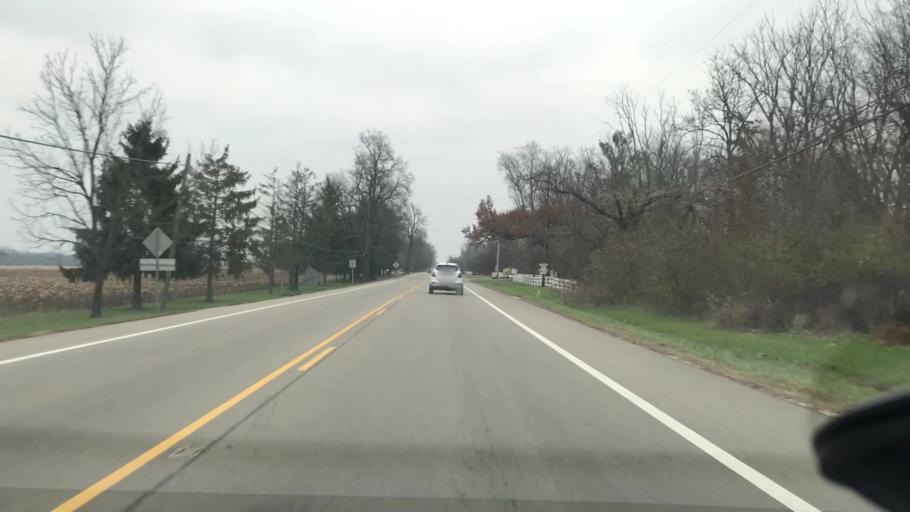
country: US
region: Ohio
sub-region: Greene County
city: Yellow Springs
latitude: 39.8124
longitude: -83.8809
